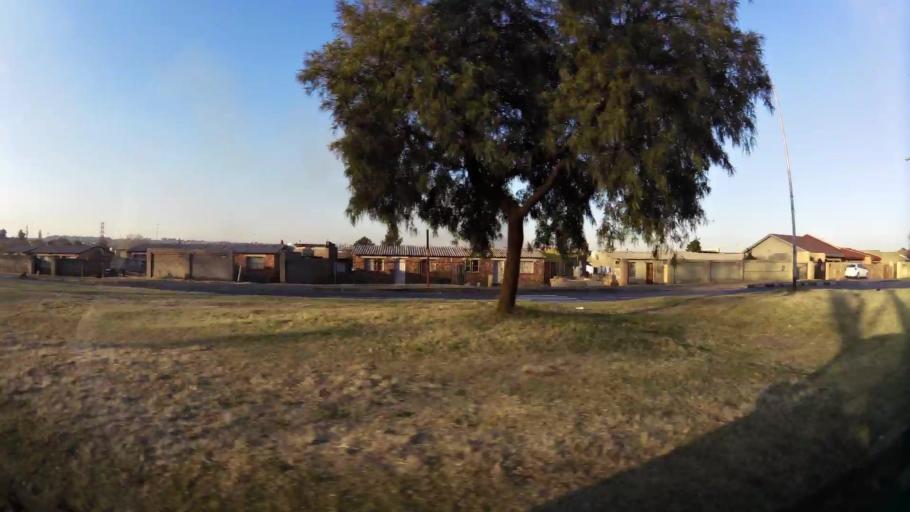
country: ZA
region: Gauteng
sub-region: City of Johannesburg Metropolitan Municipality
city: Soweto
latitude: -26.2421
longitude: 27.8803
